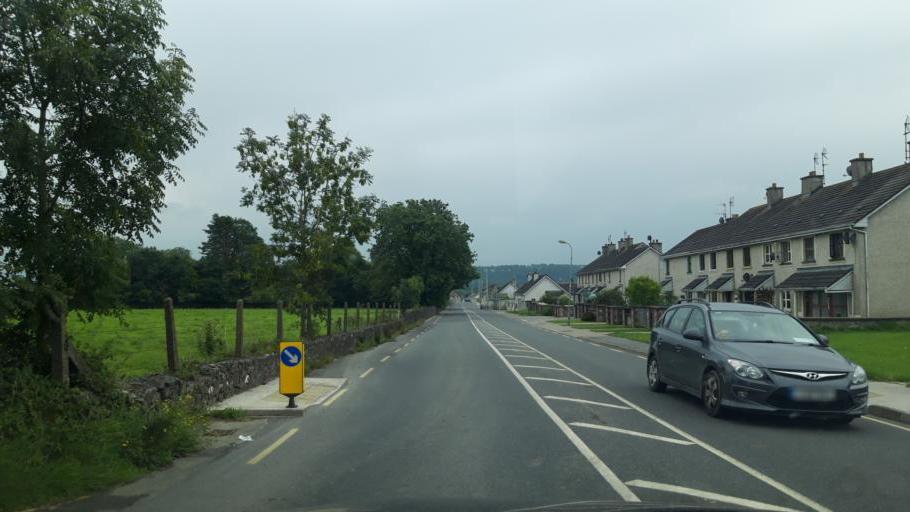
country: IE
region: Munster
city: Fethard
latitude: 52.4709
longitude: -7.6916
